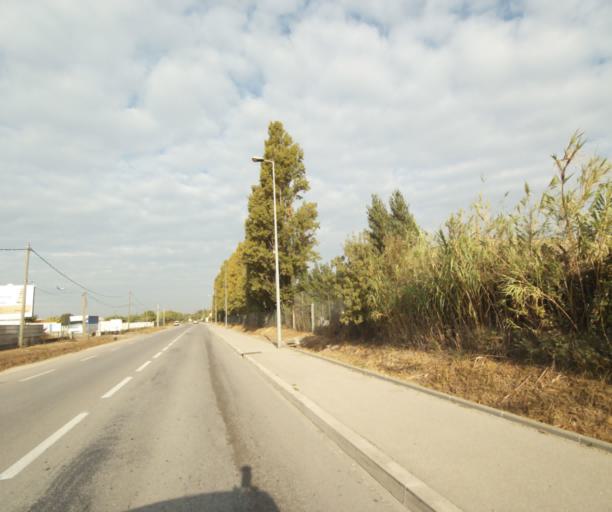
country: FR
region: Provence-Alpes-Cote d'Azur
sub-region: Departement des Bouches-du-Rhone
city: Saint-Victoret
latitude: 43.4167
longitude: 5.2625
